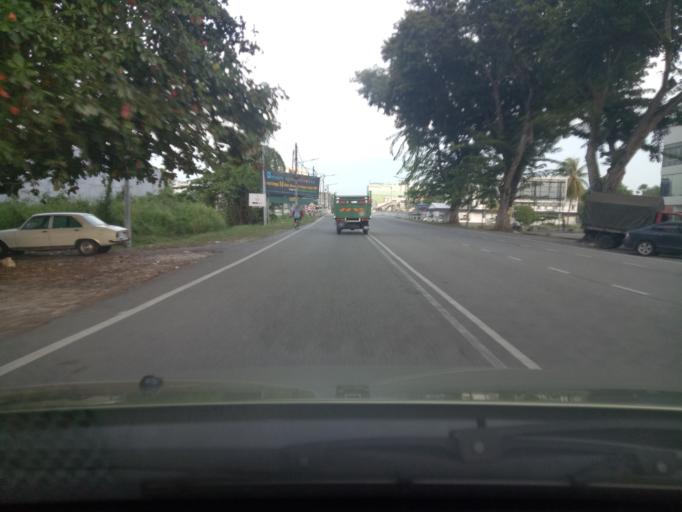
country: MY
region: Kedah
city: Alor Setar
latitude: 6.1246
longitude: 100.3589
